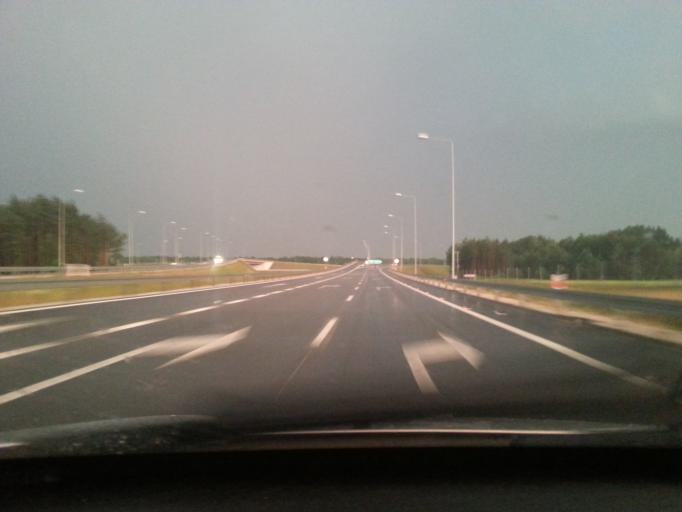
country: PL
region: Lodz Voivodeship
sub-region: Powiat pabianicki
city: Dobron
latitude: 51.6034
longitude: 19.2745
